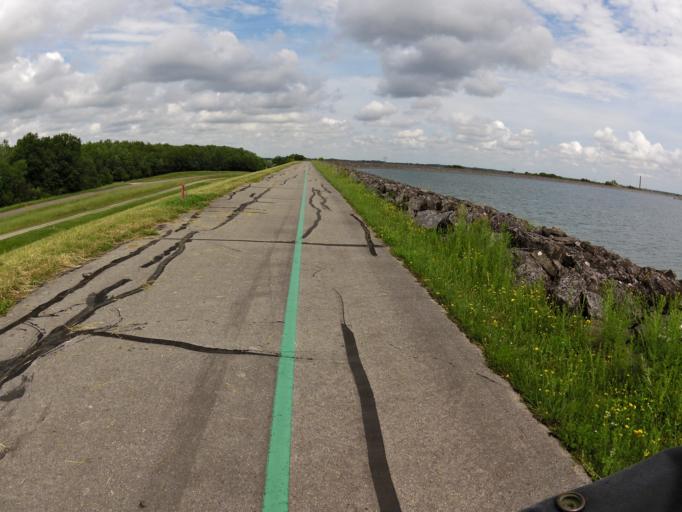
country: FR
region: Champagne-Ardenne
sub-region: Departement de l'Aube
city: Piney
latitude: 48.3371
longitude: 4.3920
